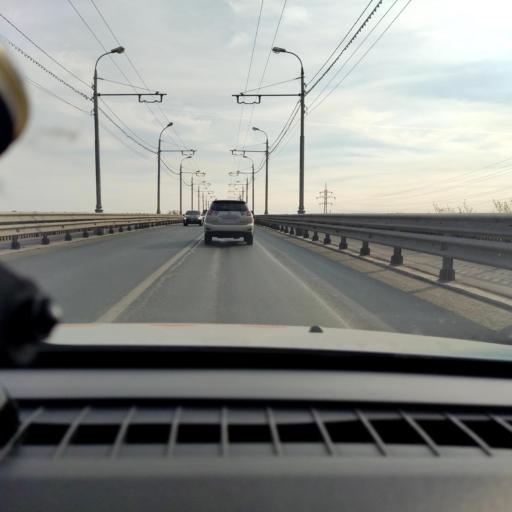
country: RU
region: Samara
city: Rozhdestveno
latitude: 53.1740
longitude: 50.0732
